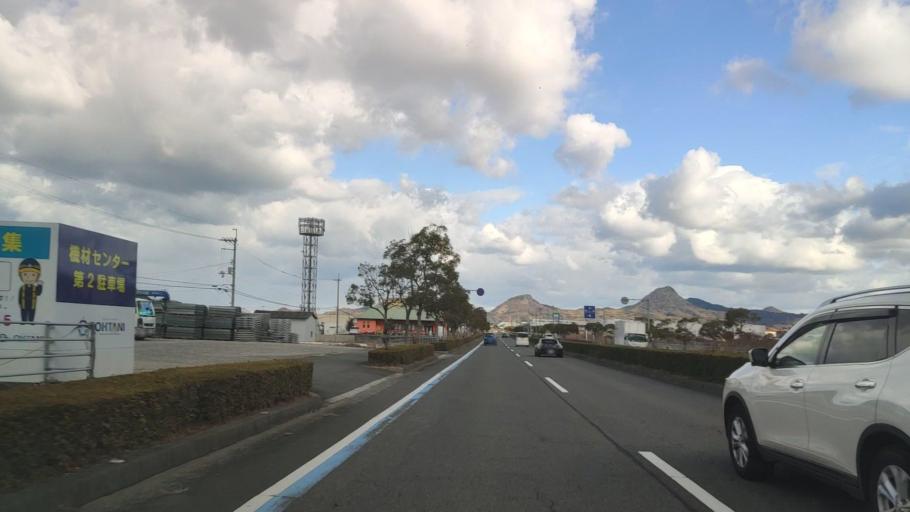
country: JP
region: Ehime
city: Hojo
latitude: 33.9569
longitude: 132.7763
